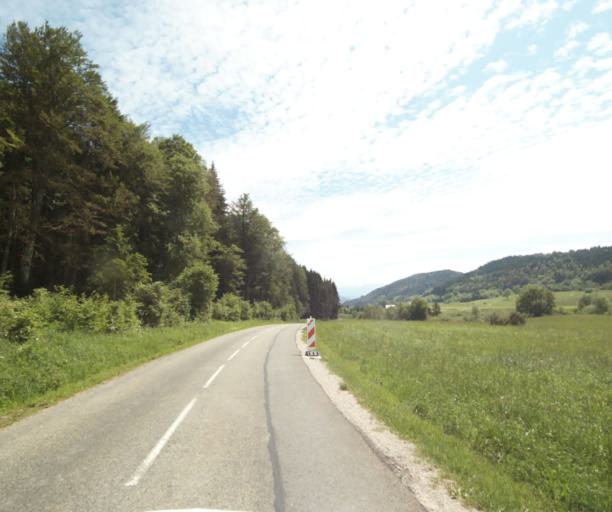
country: FR
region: Rhone-Alpes
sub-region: Departement de la Haute-Savoie
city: Perrignier
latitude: 46.2765
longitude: 6.4677
